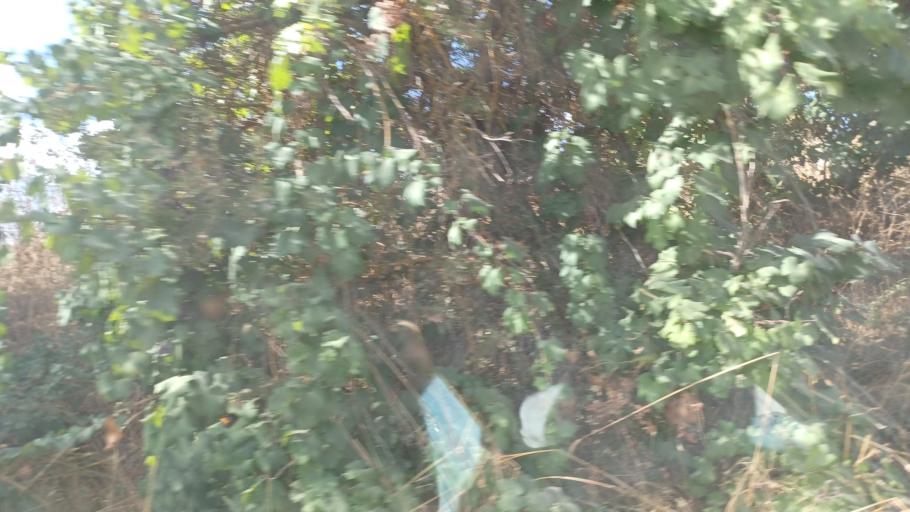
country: CY
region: Pafos
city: Mesogi
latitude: 34.8412
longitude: 32.5490
